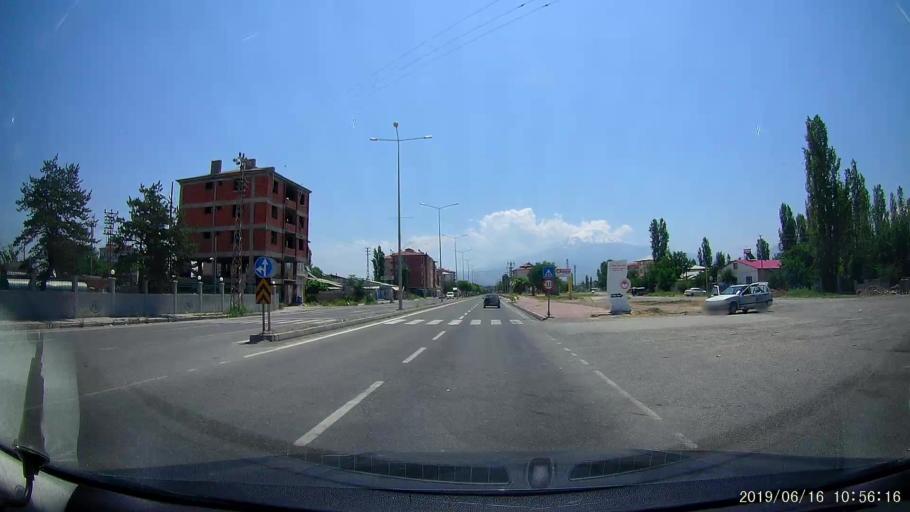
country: TR
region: Igdir
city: Igdir
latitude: 39.9309
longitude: 44.0203
